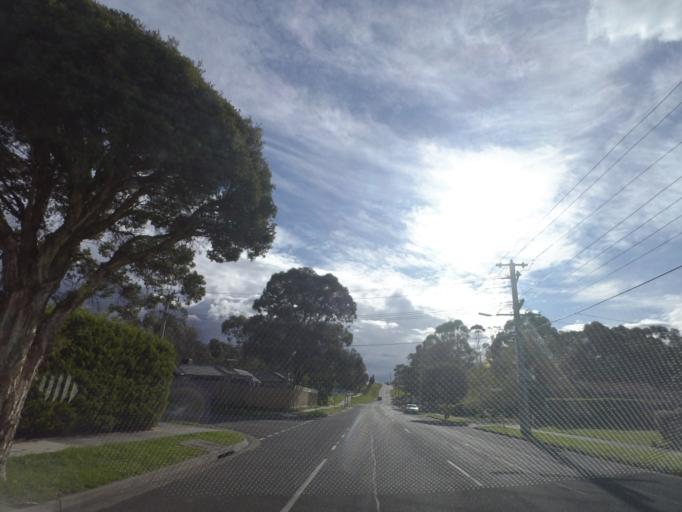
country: AU
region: Victoria
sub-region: Yarra Ranges
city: Lilydale
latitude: -37.7485
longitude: 145.3621
